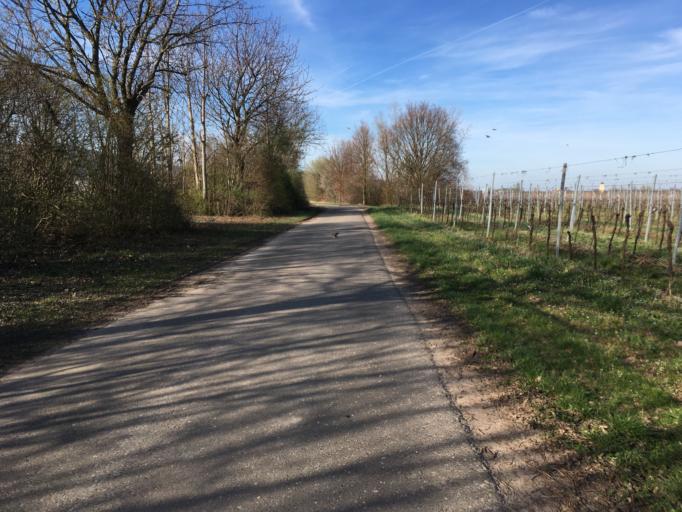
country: DE
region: Rheinland-Pfalz
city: Kirrweiler
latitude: 49.3268
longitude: 8.1589
